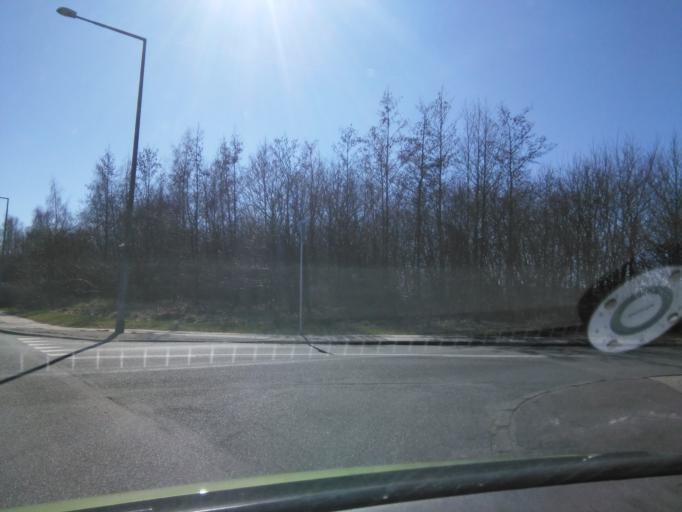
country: DK
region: Central Jutland
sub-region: Arhus Kommune
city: Lystrup
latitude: 56.2443
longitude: 10.2341
